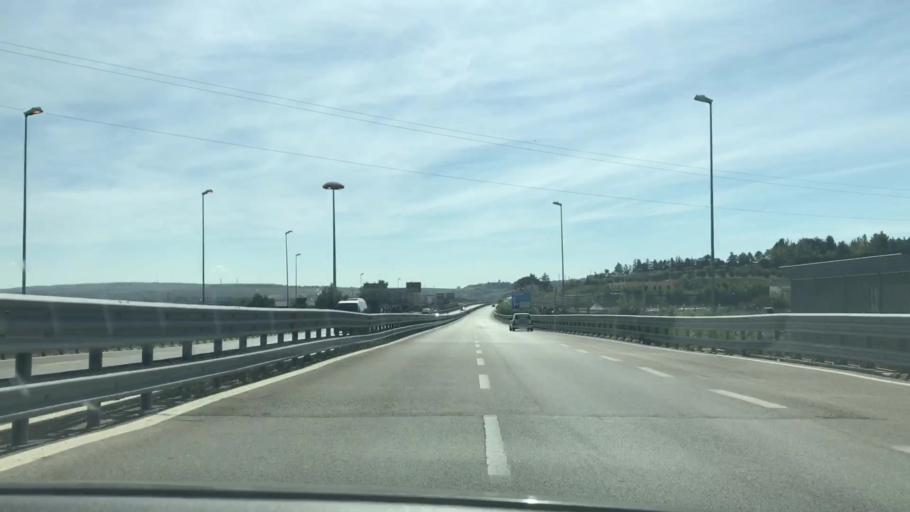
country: IT
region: Basilicate
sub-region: Provincia di Matera
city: Matera
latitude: 40.6998
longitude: 16.5879
